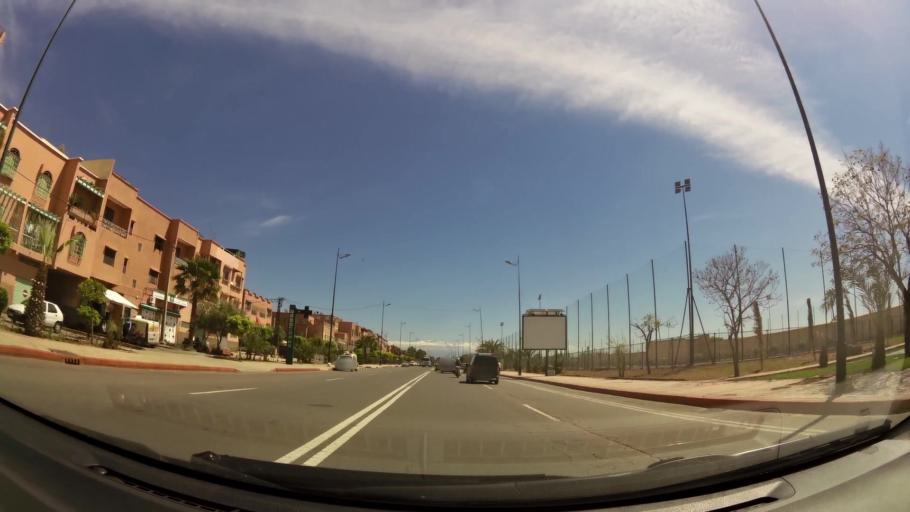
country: MA
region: Marrakech-Tensift-Al Haouz
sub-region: Marrakech
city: Marrakesh
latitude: 31.6073
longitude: -7.9731
